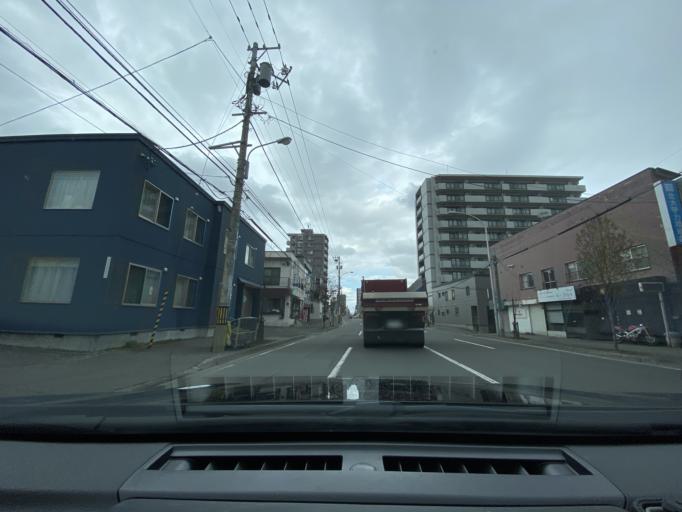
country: JP
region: Hokkaido
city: Sapporo
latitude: 43.0684
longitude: 141.2948
